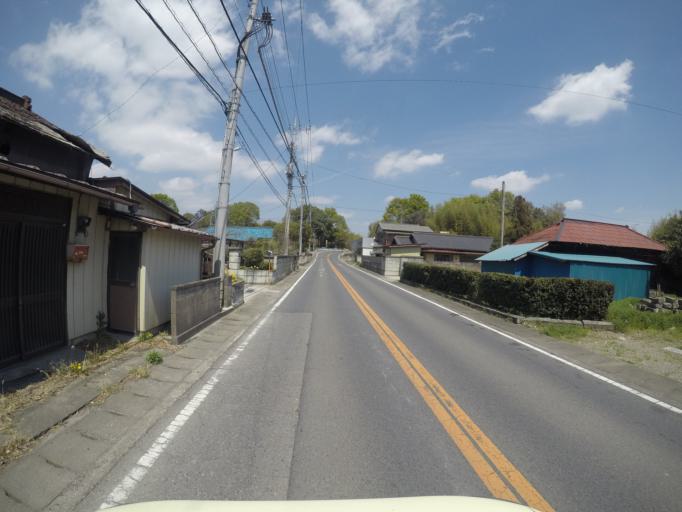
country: JP
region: Tochigi
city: Mibu
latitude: 36.4149
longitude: 139.7863
